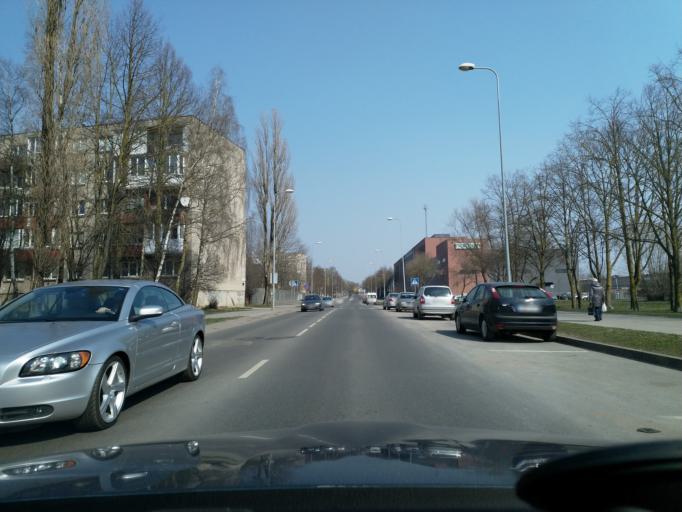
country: LT
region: Klaipedos apskritis
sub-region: Klaipeda
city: Klaipeda
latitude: 55.6965
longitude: 21.1587
